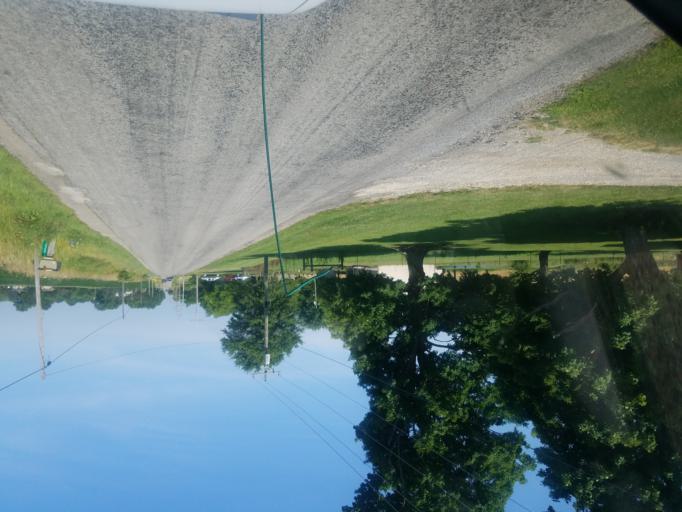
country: US
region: Ohio
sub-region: Union County
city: Marysville
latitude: 40.2895
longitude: -83.3404
